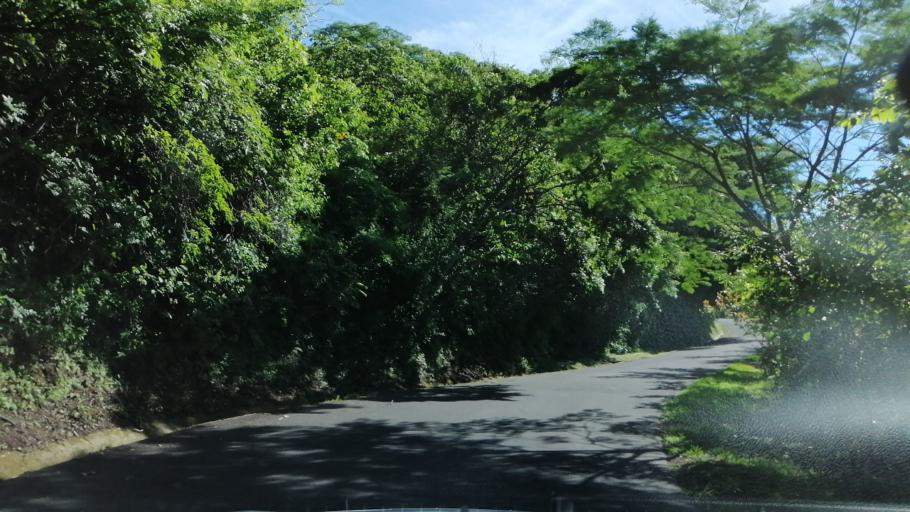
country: SV
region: Morazan
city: Corinto
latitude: 13.8076
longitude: -88.0031
